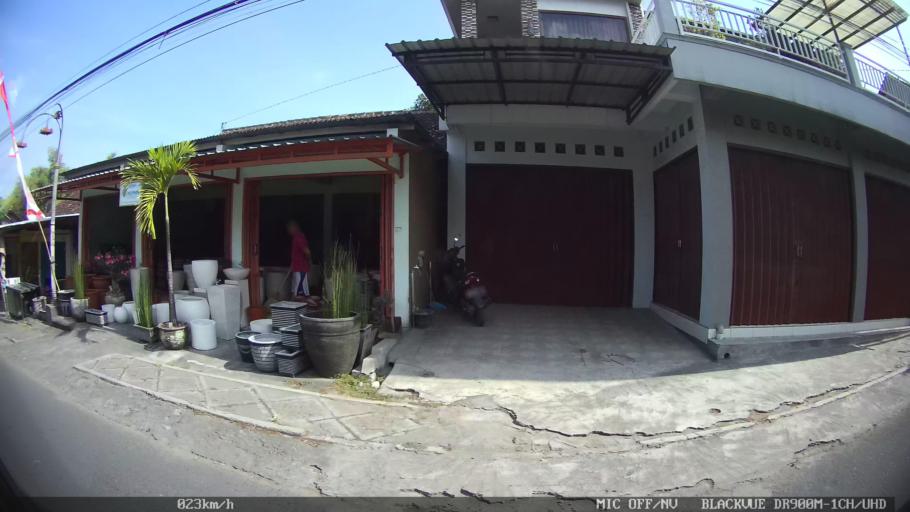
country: ID
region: Daerah Istimewa Yogyakarta
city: Kasihan
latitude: -7.8453
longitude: 110.3372
